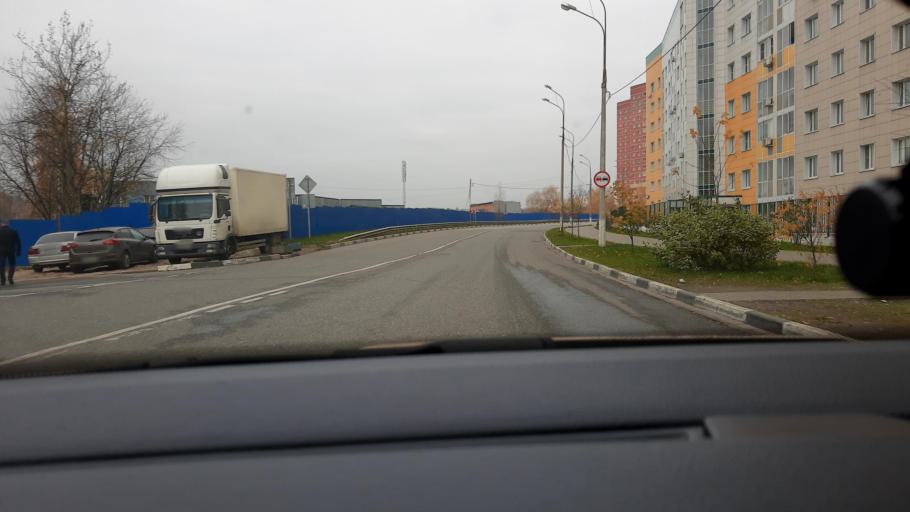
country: RU
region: Moskovskaya
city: Cherkizovo
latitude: 55.9433
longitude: 37.7732
